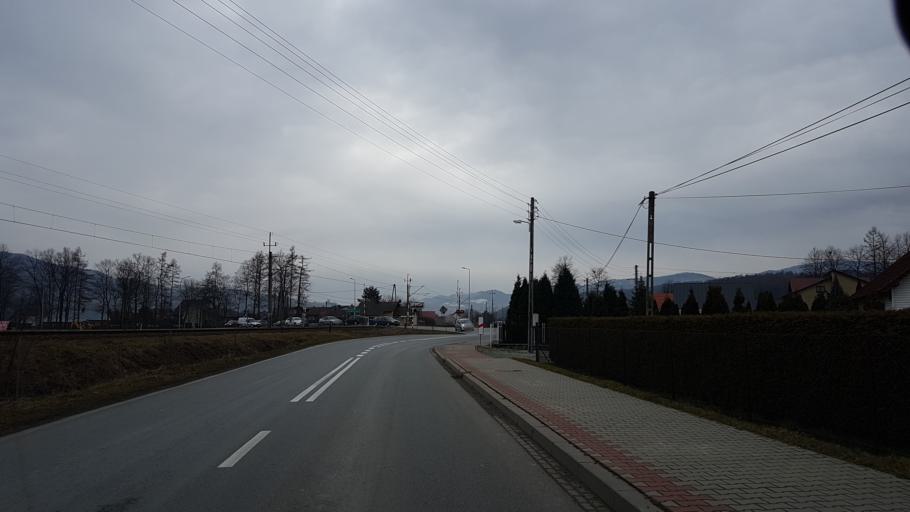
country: PL
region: Lesser Poland Voivodeship
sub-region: Powiat nowosadecki
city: Stary Sacz
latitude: 49.5395
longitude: 20.6456
